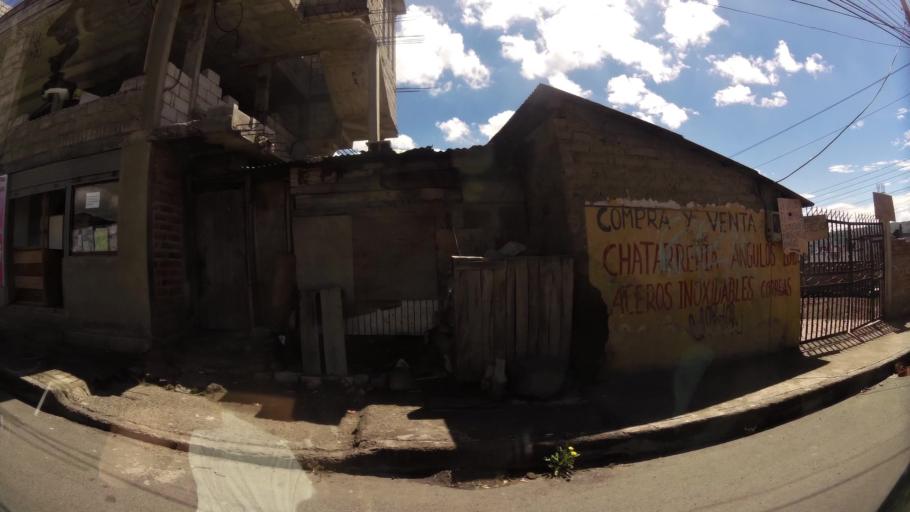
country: EC
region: Pichincha
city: Quito
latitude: -0.3150
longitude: -78.5585
